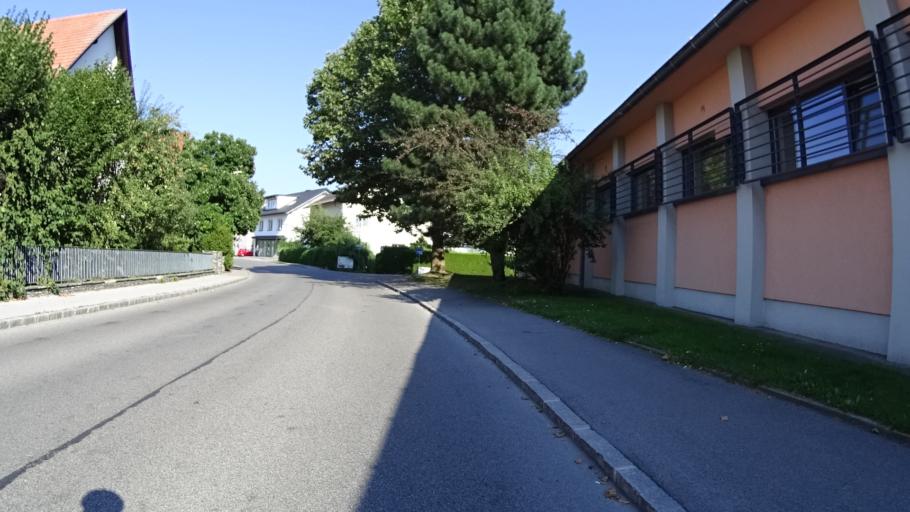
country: AT
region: Carinthia
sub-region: Villach Stadt
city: Villach
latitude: 46.6103
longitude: 13.8567
